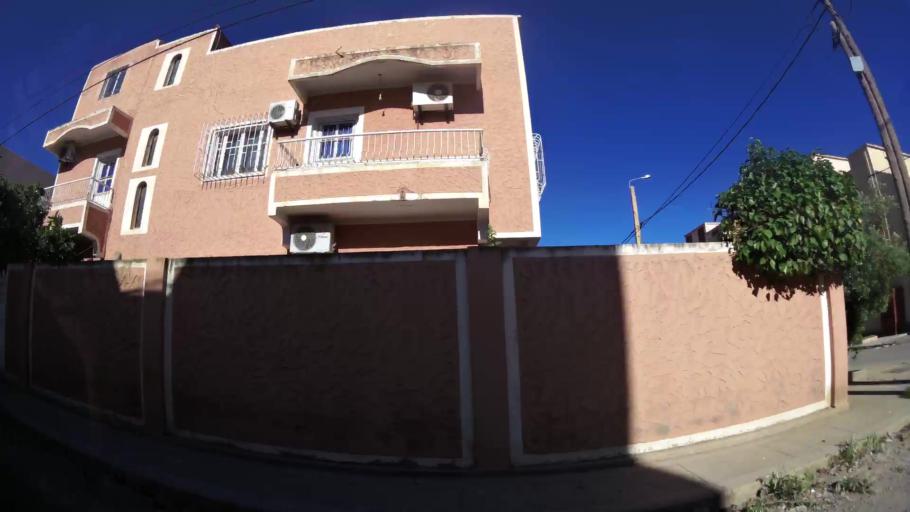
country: MA
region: Oriental
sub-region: Oujda-Angad
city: Oujda
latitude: 34.6583
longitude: -1.9003
